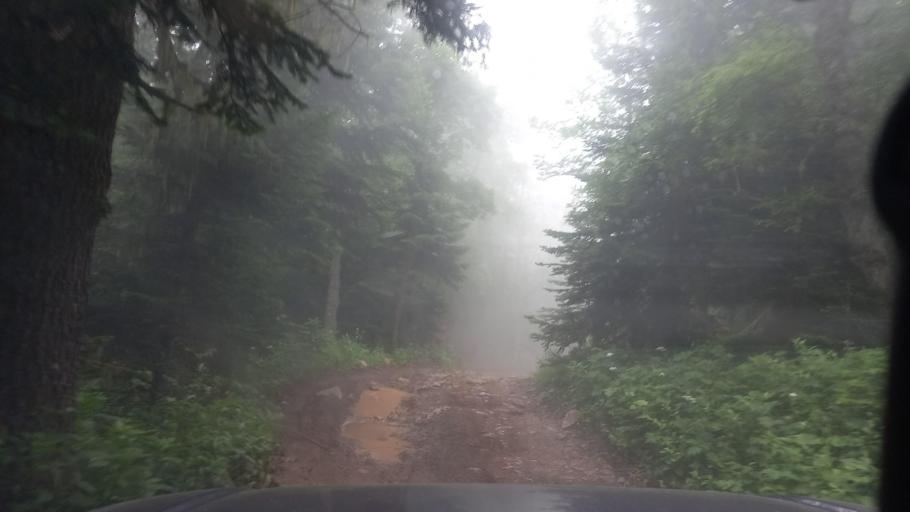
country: RU
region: Karachayevo-Cherkesiya
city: Kurdzhinovo
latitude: 43.7988
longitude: 40.8447
